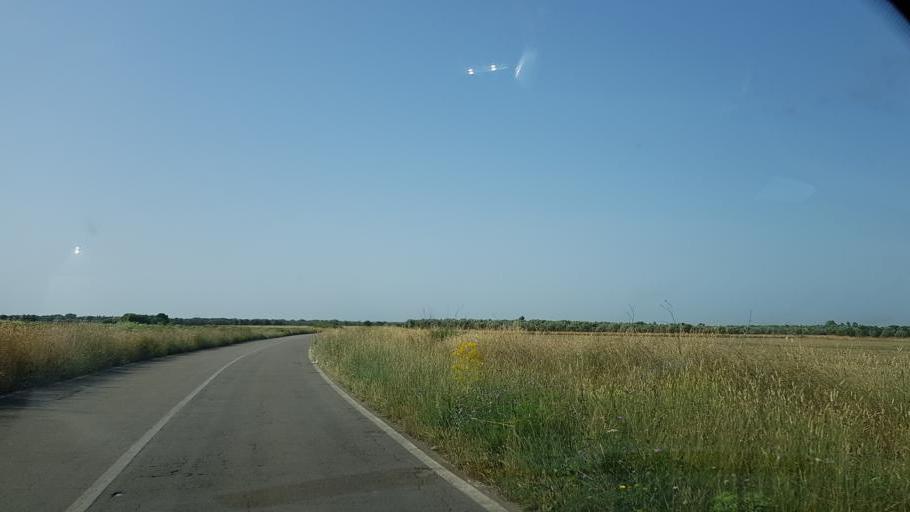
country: IT
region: Apulia
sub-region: Provincia di Brindisi
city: Mesagne
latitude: 40.5270
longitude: 17.8205
